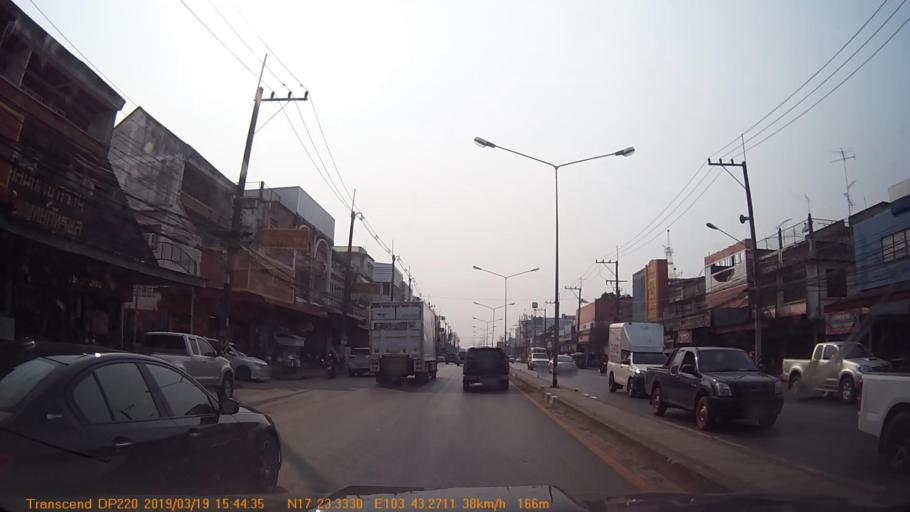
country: TH
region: Sakon Nakhon
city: Phang Khon
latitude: 17.3889
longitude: 103.7211
